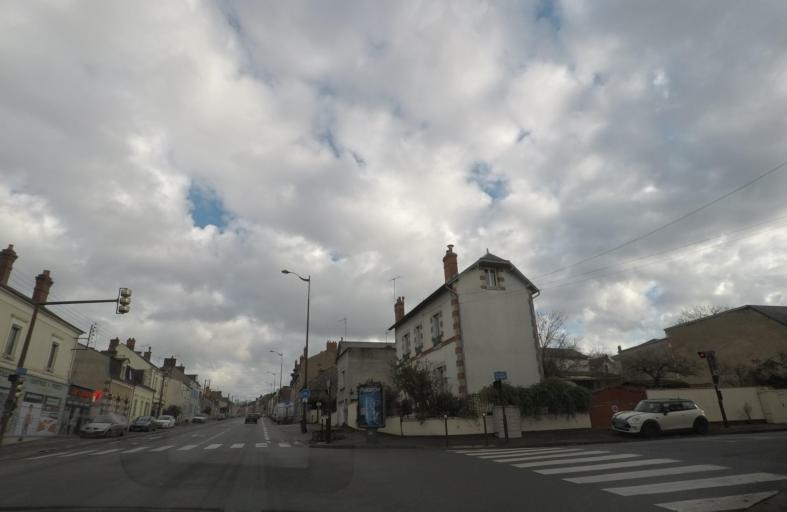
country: FR
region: Centre
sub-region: Departement du Cher
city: Bourges
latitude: 47.0726
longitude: 2.3984
